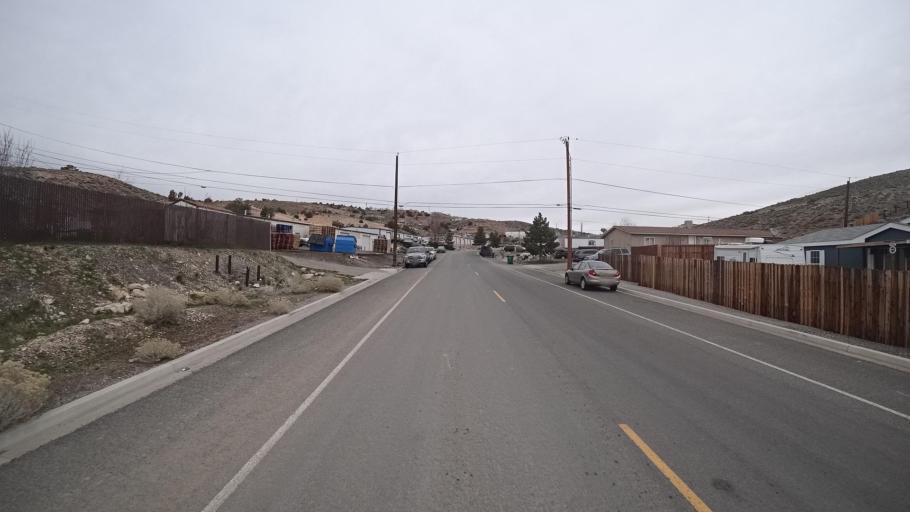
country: US
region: Nevada
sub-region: Washoe County
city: Sun Valley
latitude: 39.5999
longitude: -119.7902
